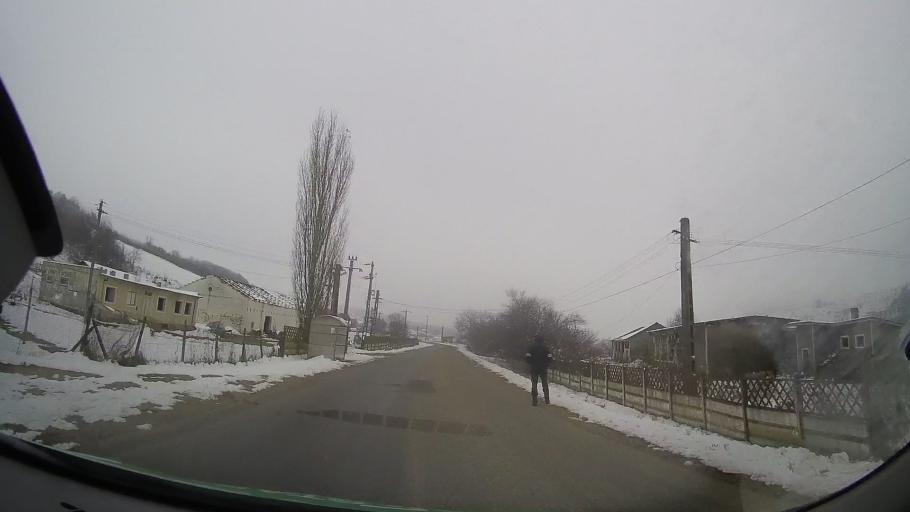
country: RO
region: Bacau
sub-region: Comuna Vultureni
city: Vultureni
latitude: 46.3698
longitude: 27.2822
